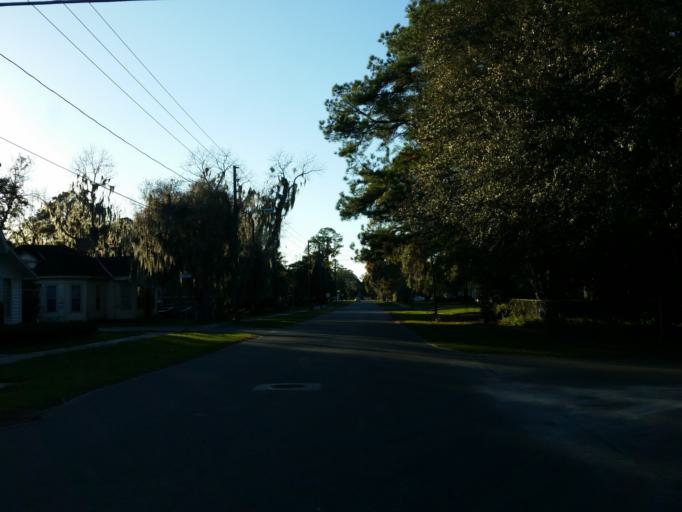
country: US
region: Florida
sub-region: Hamilton County
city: Jasper
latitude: 30.5209
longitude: -82.9504
